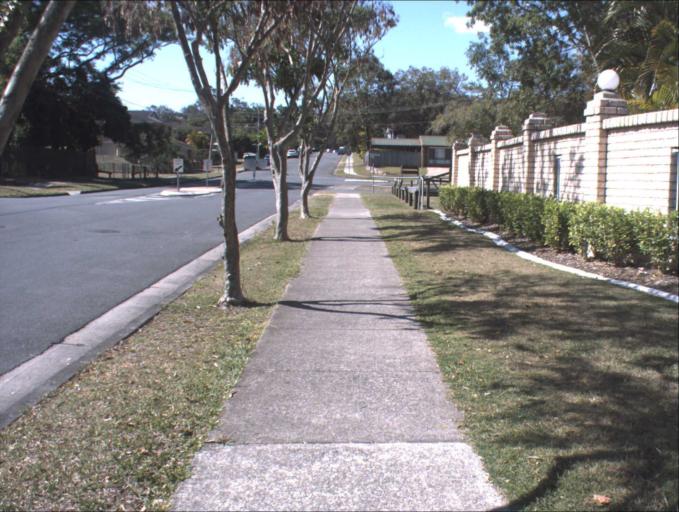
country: AU
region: Queensland
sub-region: Logan
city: Slacks Creek
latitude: -27.6319
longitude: 153.1391
